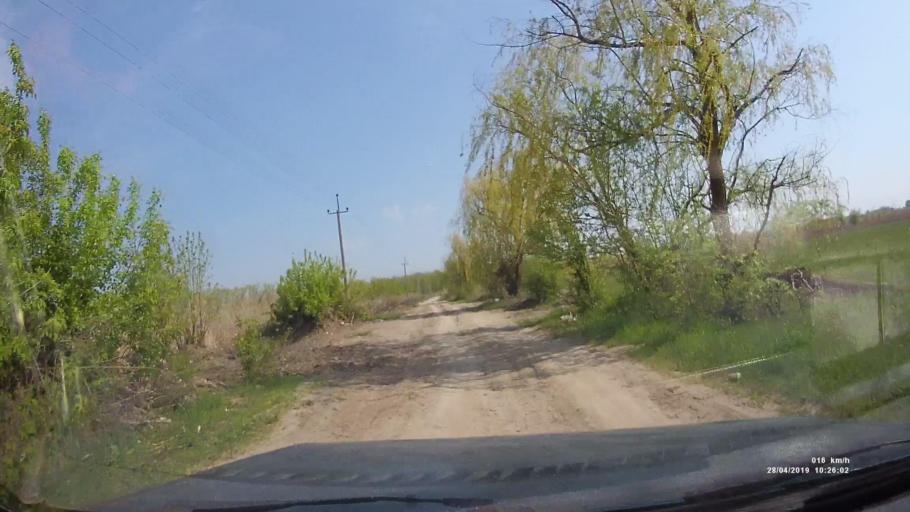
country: RU
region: Rostov
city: Azov
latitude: 47.1127
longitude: 39.4432
